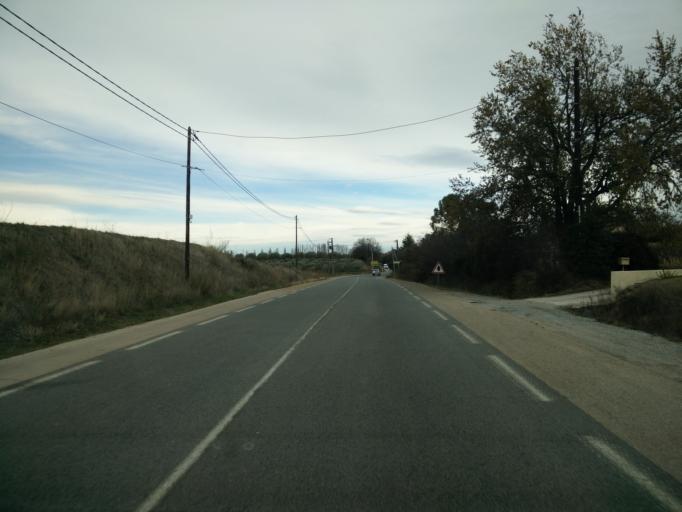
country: FR
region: Provence-Alpes-Cote d'Azur
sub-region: Departement du Var
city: Puget-sur-Argens
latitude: 43.4364
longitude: 6.6605
